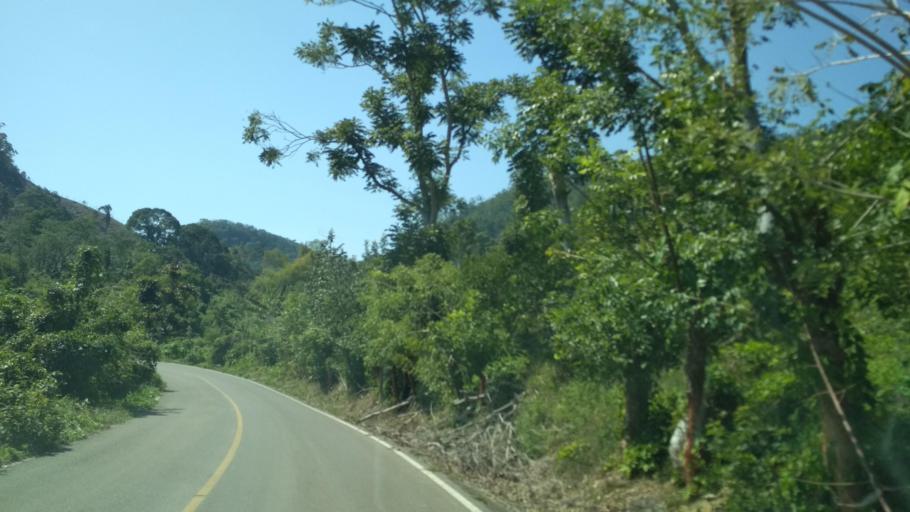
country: MX
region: Veracruz
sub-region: Papantla
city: Polutla
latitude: 20.4709
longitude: -97.2242
